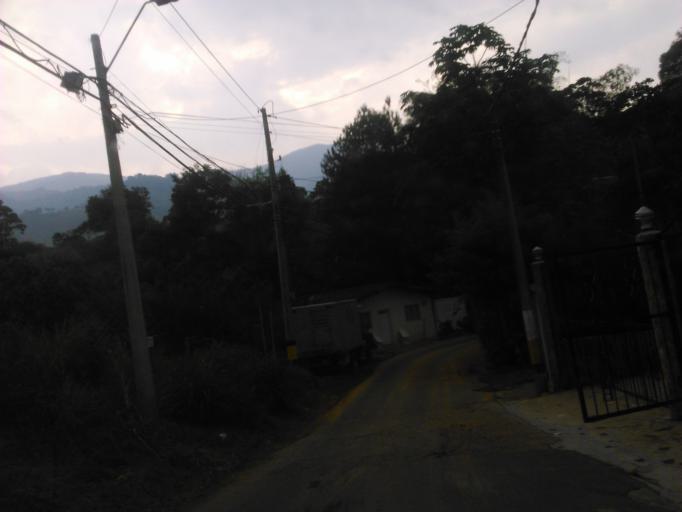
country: CO
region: Antioquia
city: La Estrella
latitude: 6.1426
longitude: -75.6379
